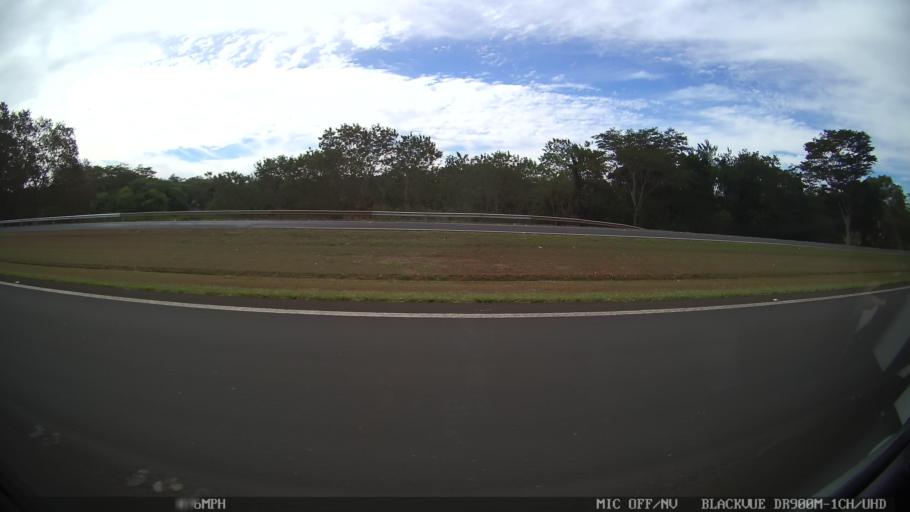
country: BR
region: Sao Paulo
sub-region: Santa Adelia
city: Santa Adelia
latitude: -21.2916
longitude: -48.8439
